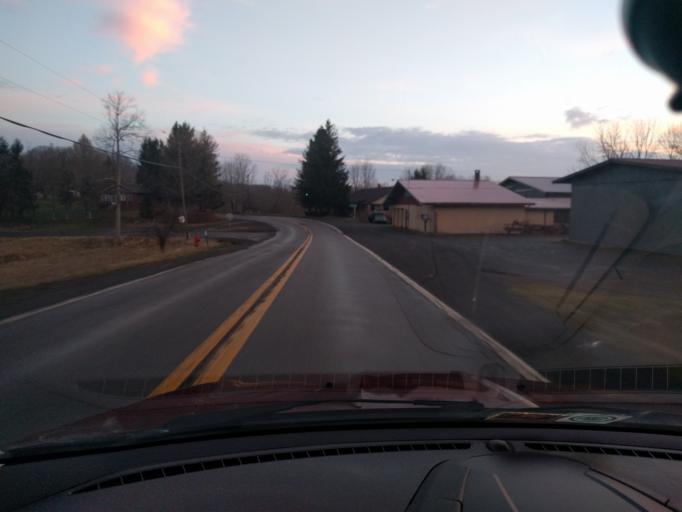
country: US
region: West Virginia
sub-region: Greenbrier County
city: Rainelle
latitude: 38.0057
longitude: -80.8791
